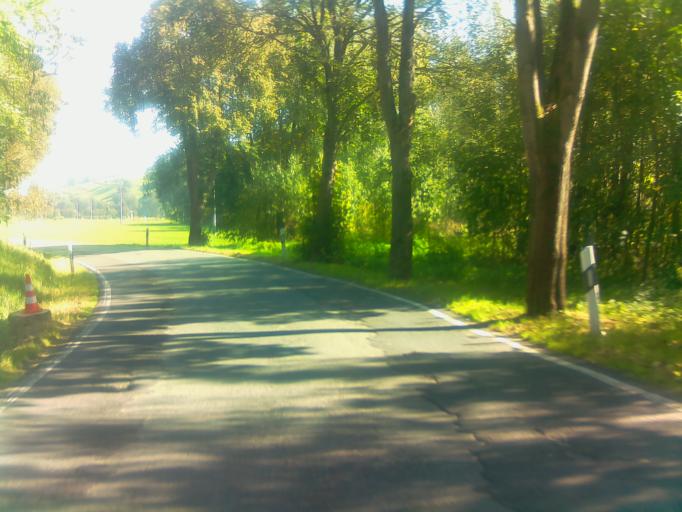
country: DE
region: Thuringia
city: Waltersdorf
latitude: 50.8325
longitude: 11.7635
